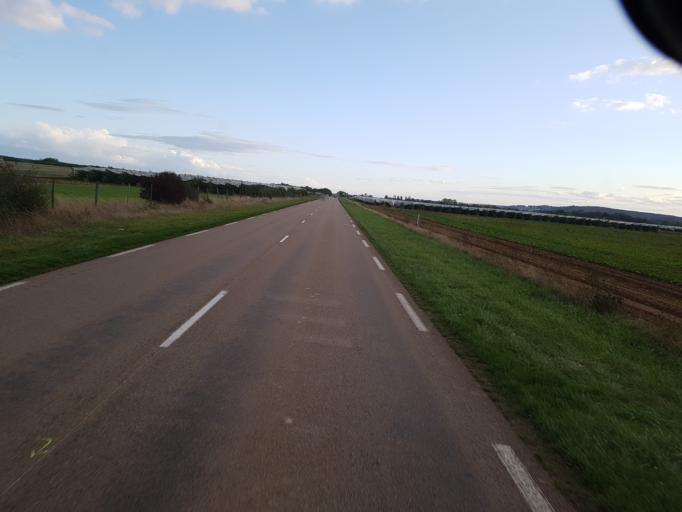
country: FR
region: Bourgogne
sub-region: Departement de l'Yonne
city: Saint-Clement
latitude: 48.2525
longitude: 3.2847
